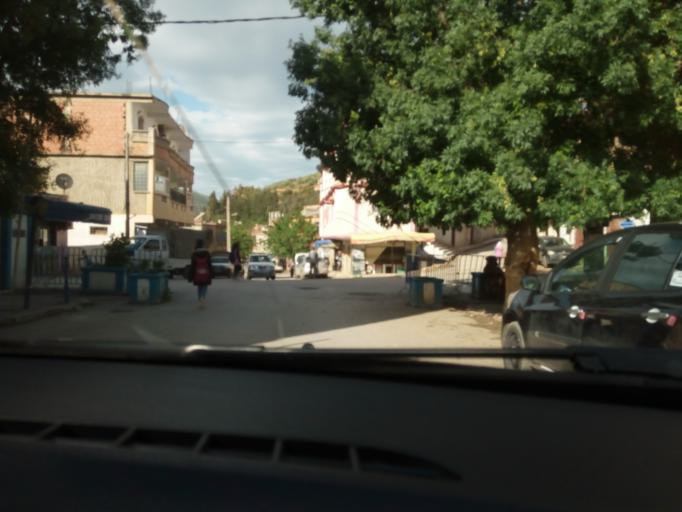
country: DZ
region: Tipaza
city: Hadjout
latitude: 36.3706
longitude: 2.4769
